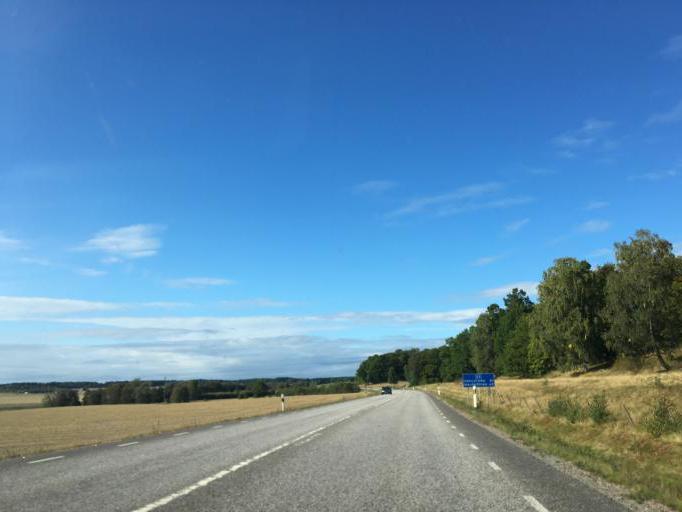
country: SE
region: Soedermanland
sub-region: Nykopings Kommun
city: Nykoping
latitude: 58.7813
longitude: 16.9664
